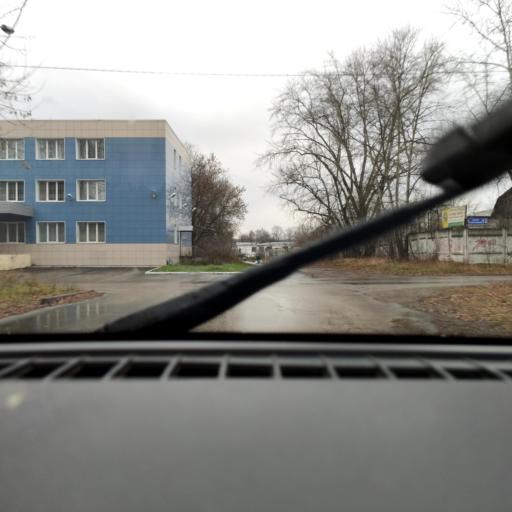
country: RU
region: Perm
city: Kultayevo
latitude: 57.9973
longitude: 55.9341
